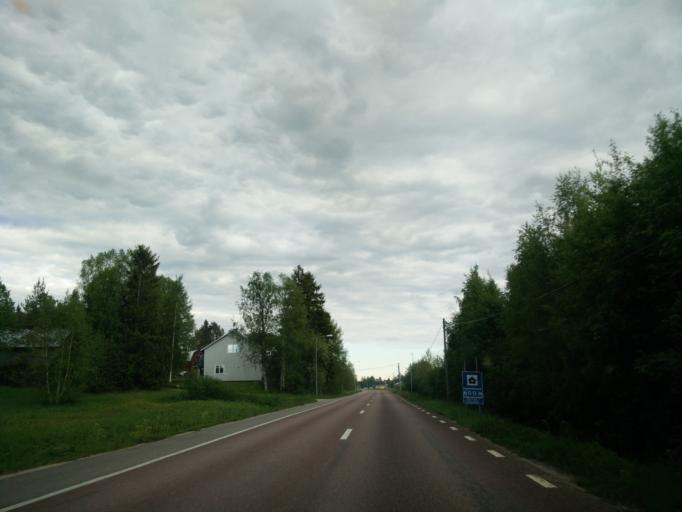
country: SE
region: Jaemtland
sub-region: Harjedalens Kommun
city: Sveg
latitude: 62.2886
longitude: 14.7947
